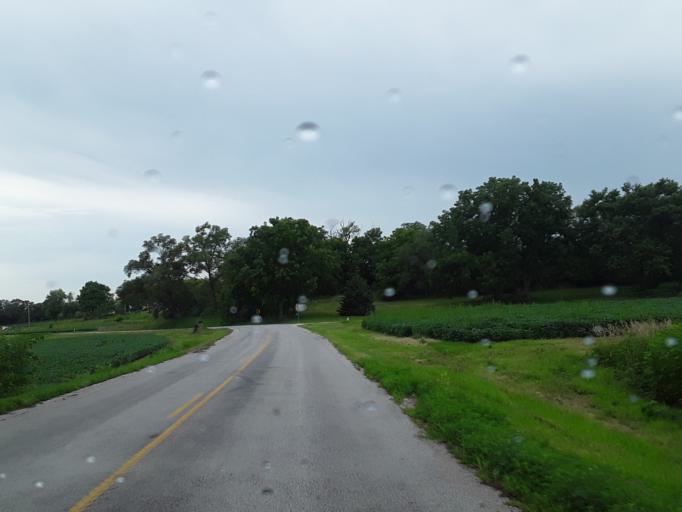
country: US
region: Nebraska
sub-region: Washington County
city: Blair
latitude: 41.5019
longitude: -96.1582
